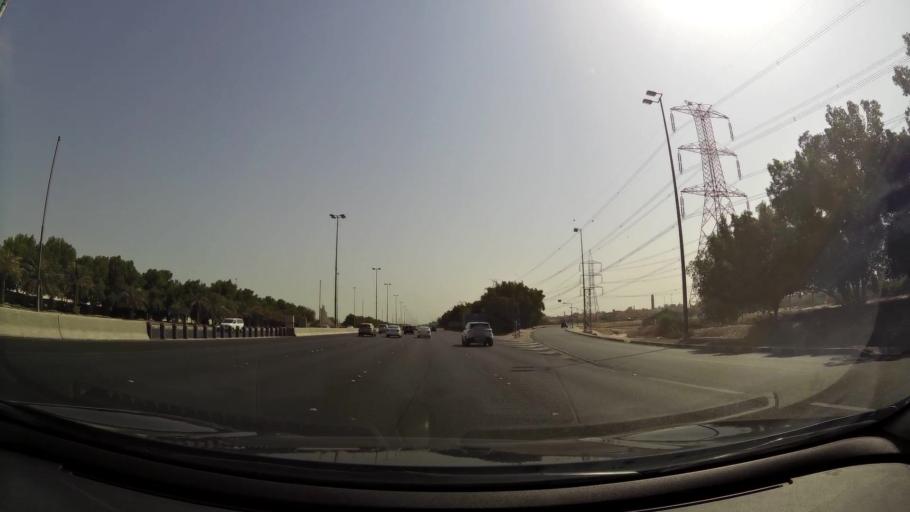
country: KW
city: Bayan
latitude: 29.2930
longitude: 48.0280
